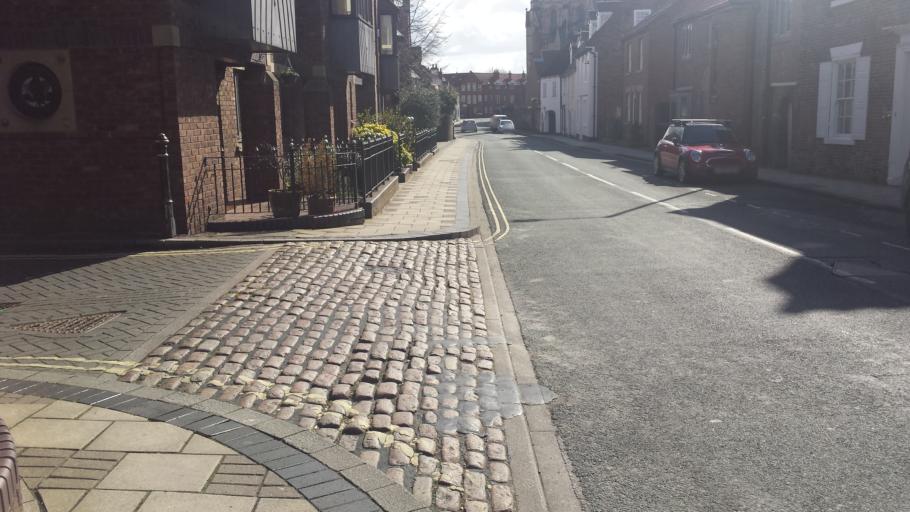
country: GB
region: England
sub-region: East Riding of Yorkshire
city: Beverley
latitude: 53.8409
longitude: -0.4253
